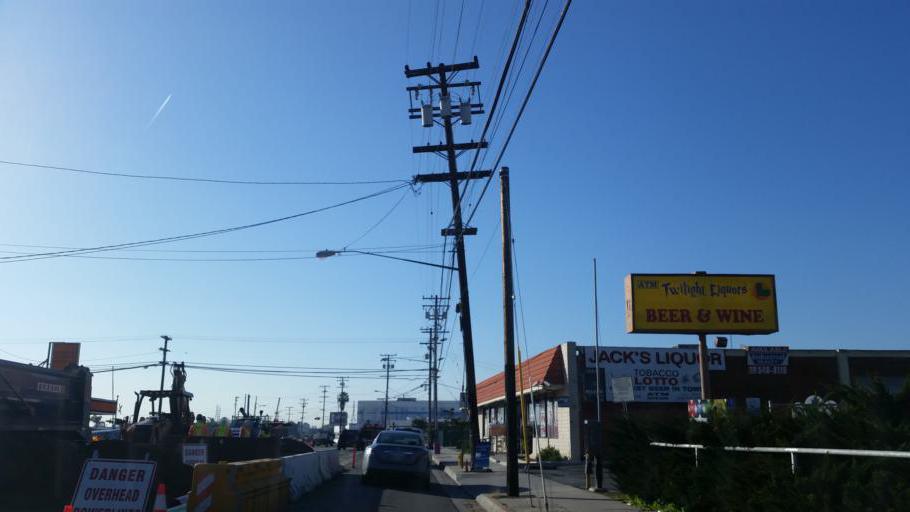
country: US
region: California
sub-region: Los Angeles County
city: Gardena
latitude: 33.8796
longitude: -118.2999
